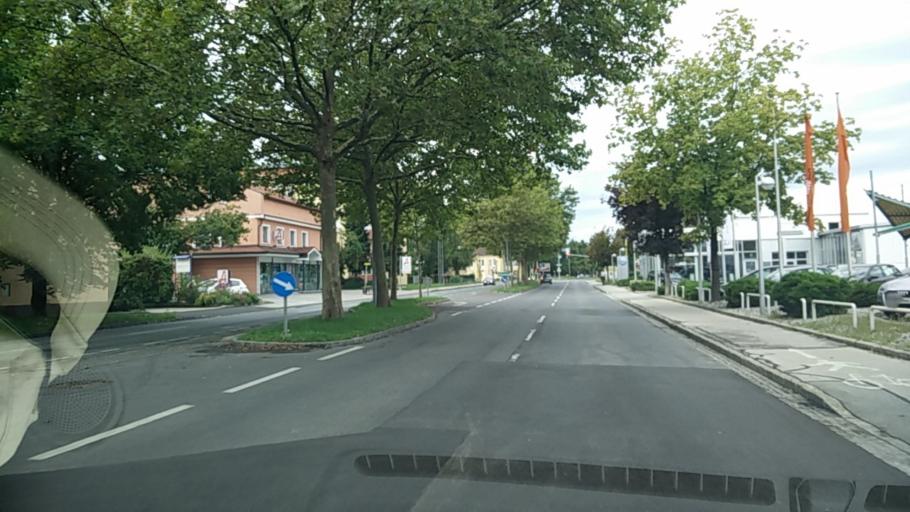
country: AT
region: Carinthia
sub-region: Politischer Bezirk Klagenfurt Land
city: Ebenthal
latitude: 46.6255
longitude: 14.3383
